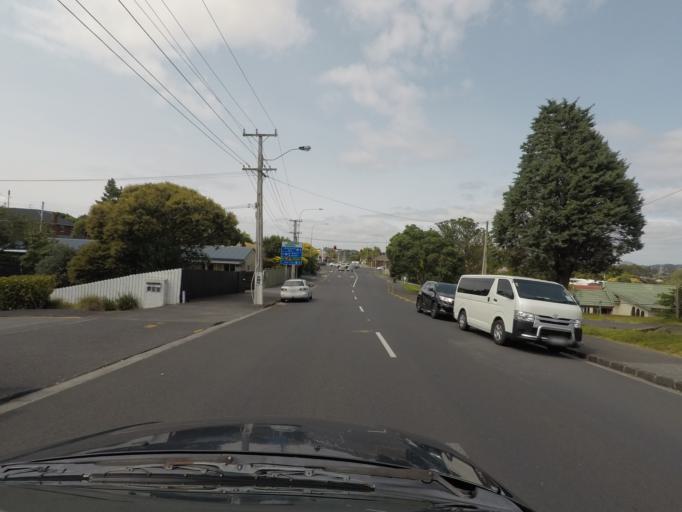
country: NZ
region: Auckland
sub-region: Auckland
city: Rosebank
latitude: -36.9047
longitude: 174.7016
